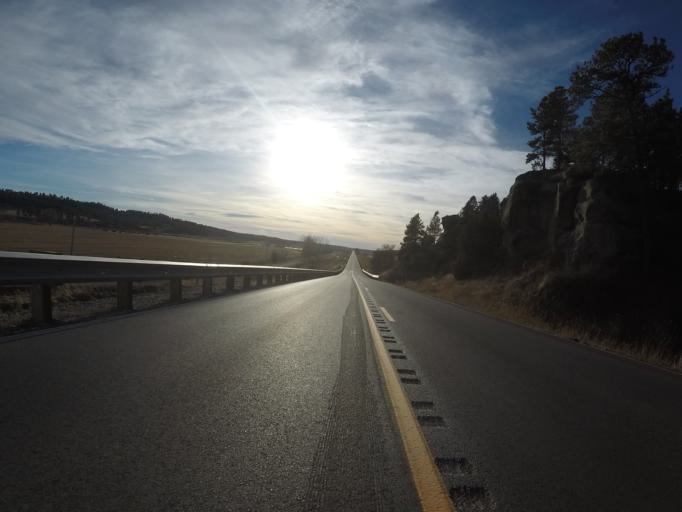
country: US
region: Montana
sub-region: Musselshell County
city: Roundup
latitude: 46.3977
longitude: -108.6060
